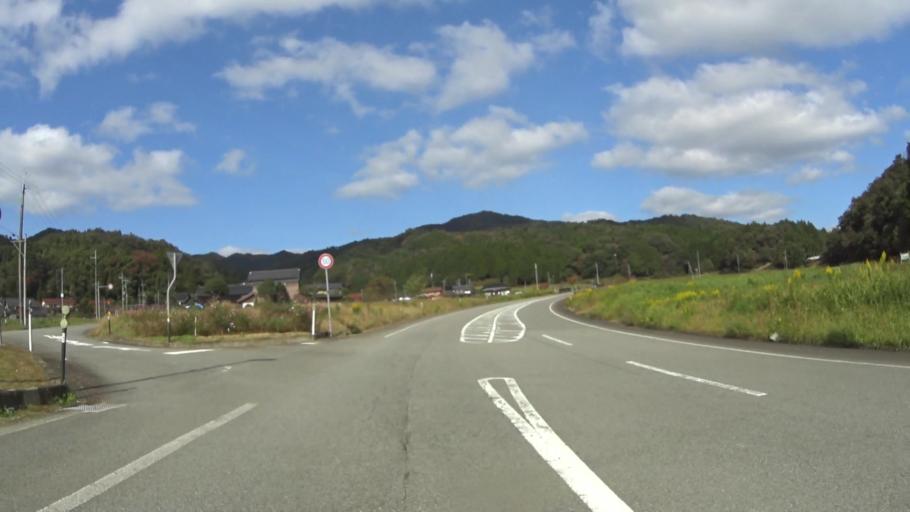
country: JP
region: Hyogo
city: Toyooka
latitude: 35.5064
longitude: 134.9910
